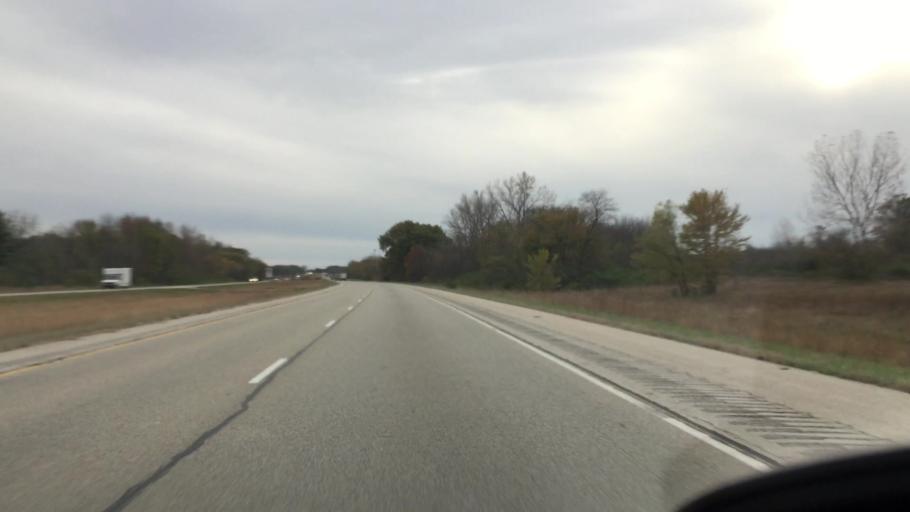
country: US
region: Illinois
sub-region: McLean County
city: Twin Grove
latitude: 40.3781
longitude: -89.0943
